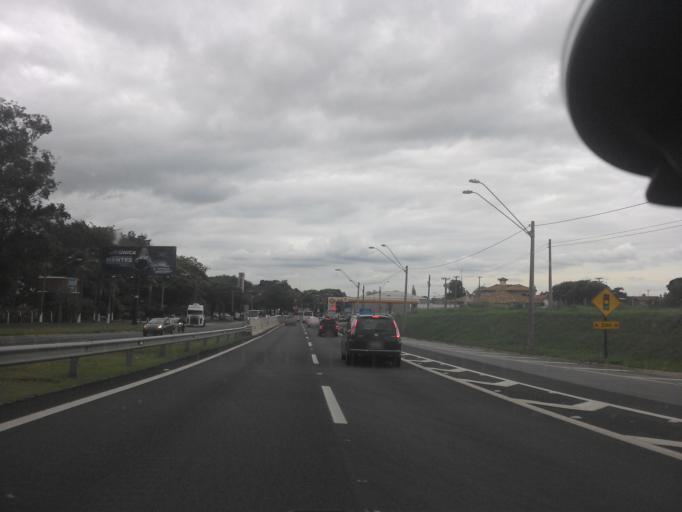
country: BR
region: Sao Paulo
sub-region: Campinas
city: Campinas
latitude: -22.8371
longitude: -47.0792
